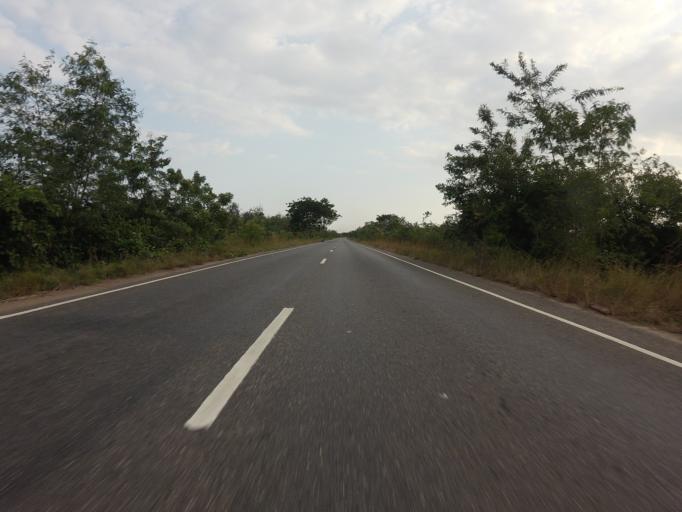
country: GH
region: Volta
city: Ho
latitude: 6.1250
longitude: 0.5219
